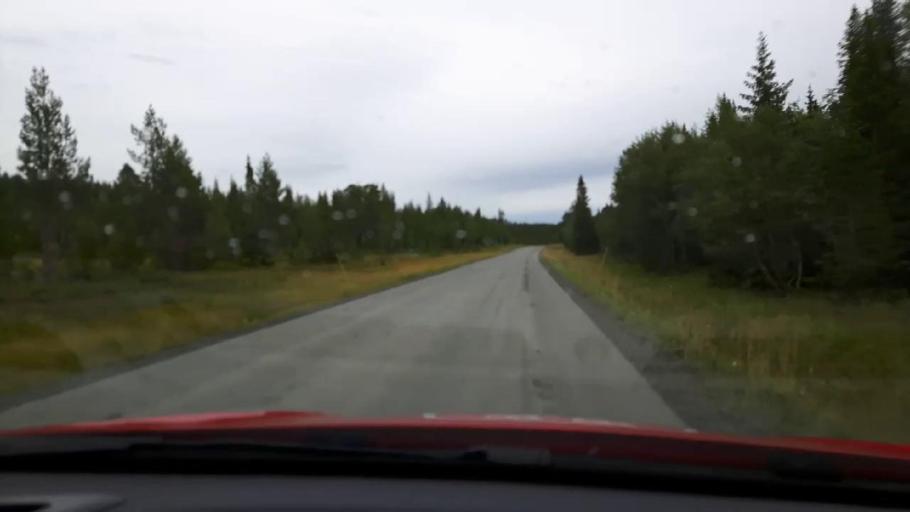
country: SE
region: Jaemtland
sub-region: Are Kommun
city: Are
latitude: 63.4394
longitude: 13.2559
